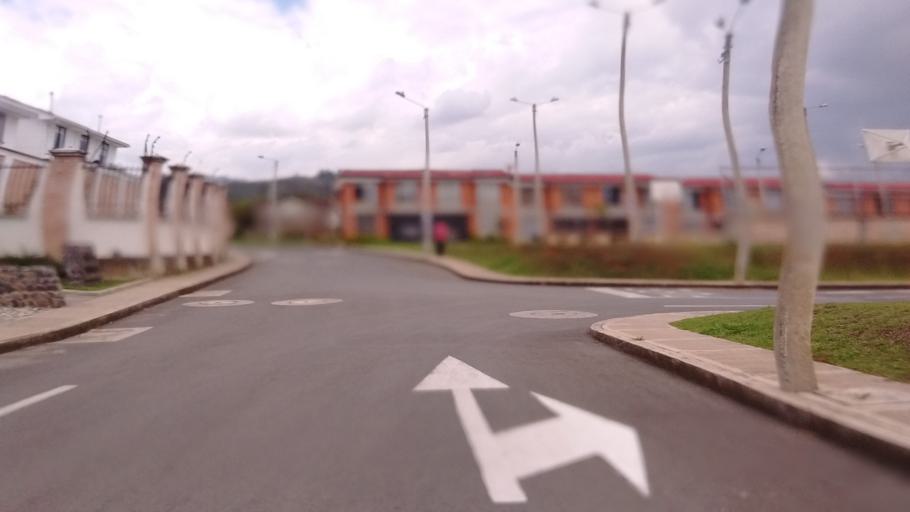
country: CO
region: Cauca
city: Popayan
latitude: 2.4626
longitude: -76.5855
